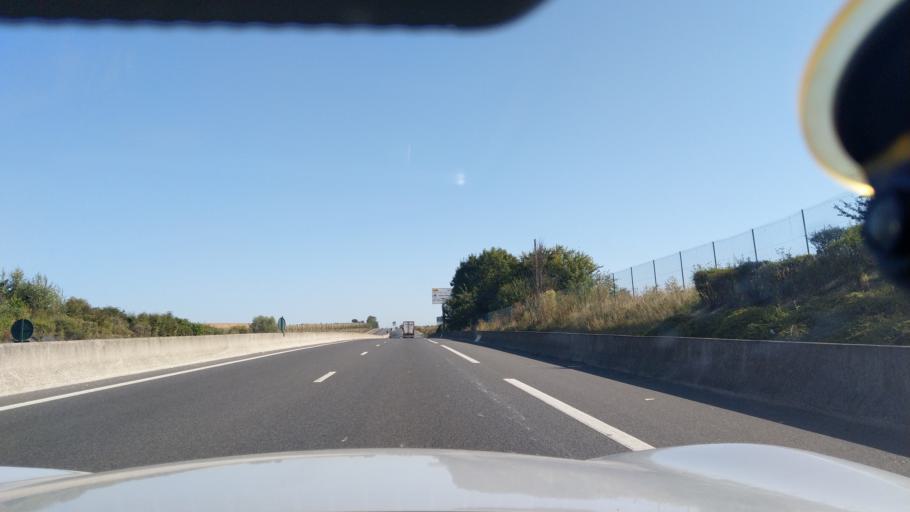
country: FR
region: Ile-de-France
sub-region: Departement du Val-d'Oise
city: Le Thillay
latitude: 48.9851
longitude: 2.4708
